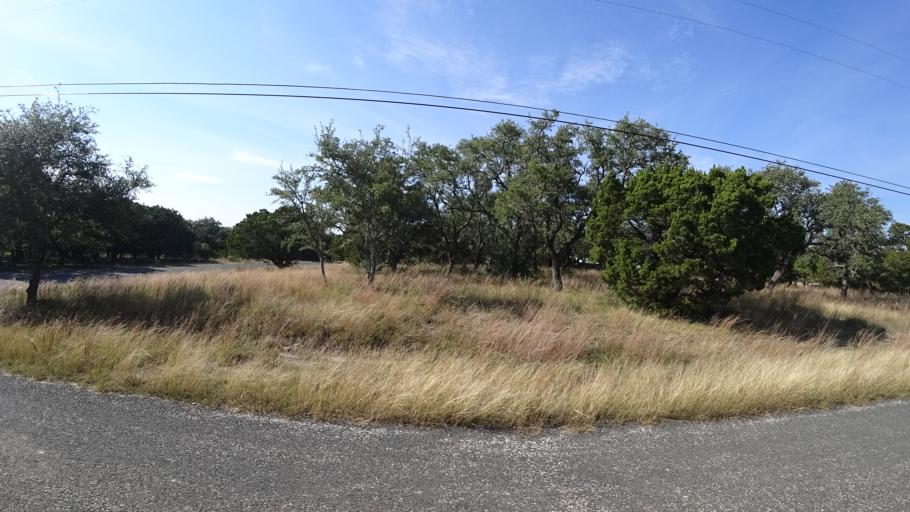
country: US
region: Texas
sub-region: Travis County
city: Barton Creek
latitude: 30.2239
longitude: -97.9088
